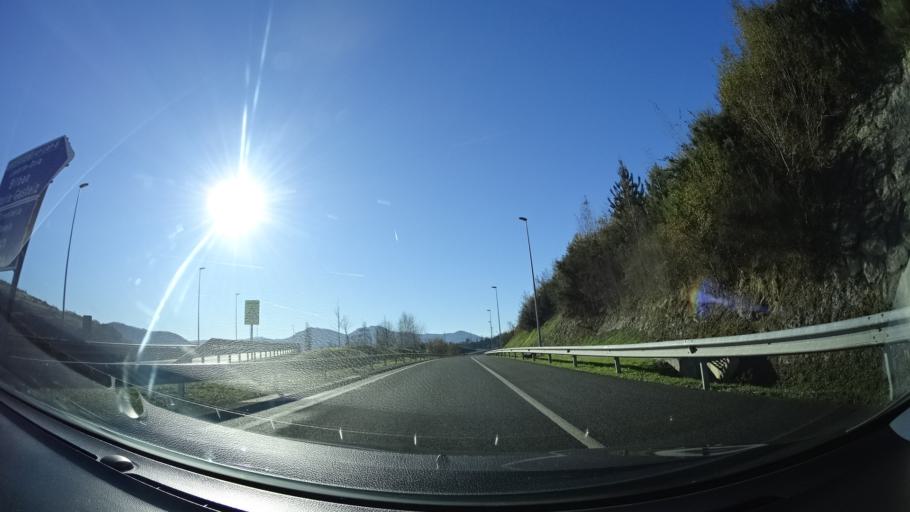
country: ES
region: Basque Country
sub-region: Provincia de Guipuzcoa
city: Astigarraga
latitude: 43.2831
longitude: -1.9600
